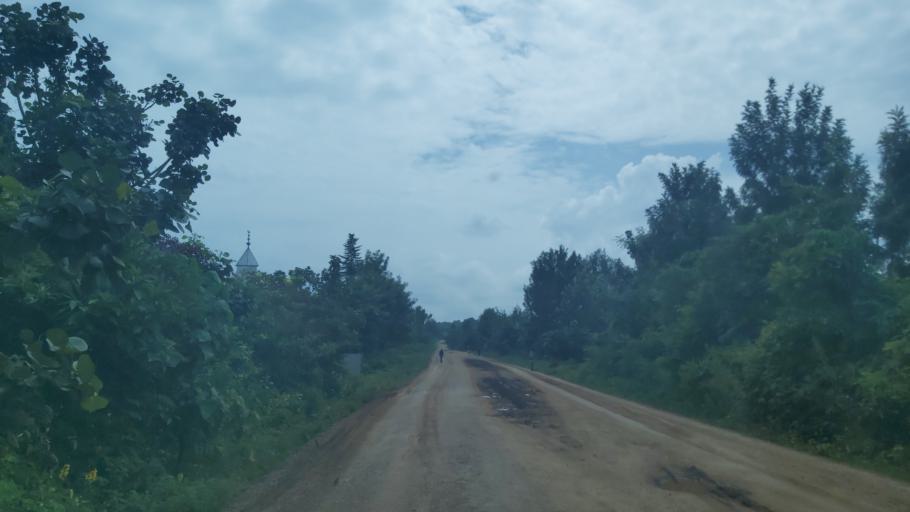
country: ET
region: Oromiya
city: Jima
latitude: 7.7418
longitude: 36.7894
